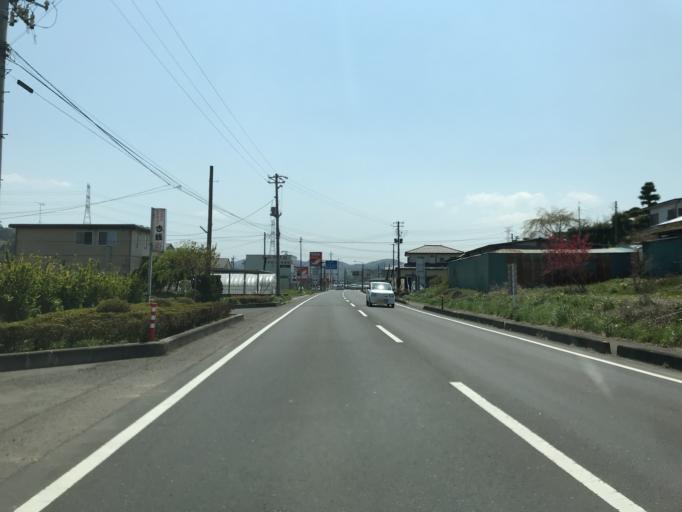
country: JP
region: Fukushima
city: Ishikawa
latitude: 37.0827
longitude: 140.4190
